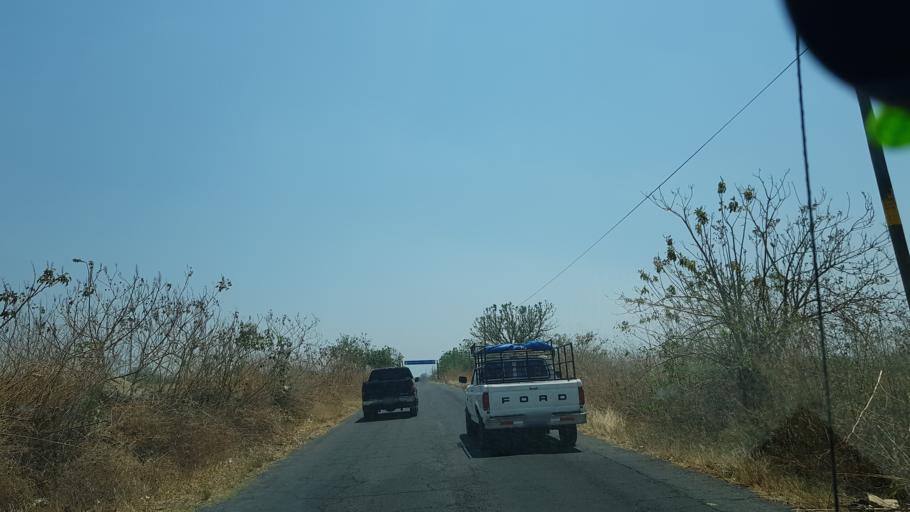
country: MX
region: Puebla
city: Tochimilco
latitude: 18.8871
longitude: -98.5447
